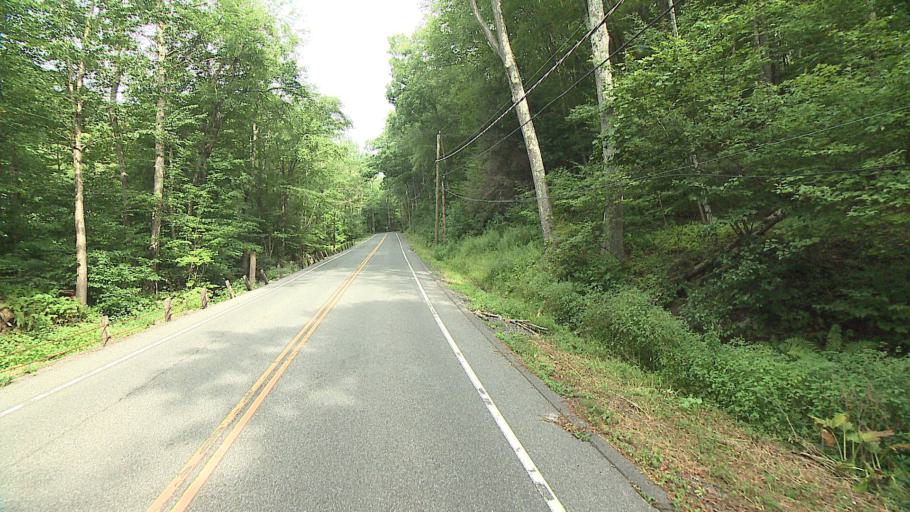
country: US
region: Connecticut
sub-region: Litchfield County
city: Bethlehem Village
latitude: 41.6006
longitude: -73.2796
